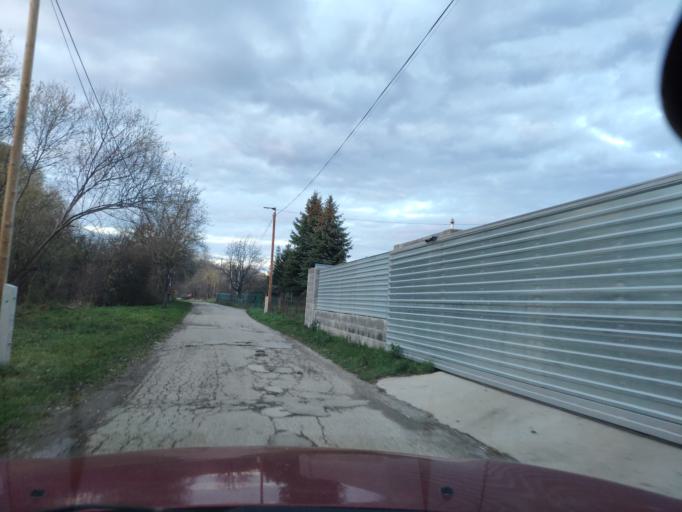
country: SK
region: Kosicky
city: Kosice
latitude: 48.6604
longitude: 21.3553
